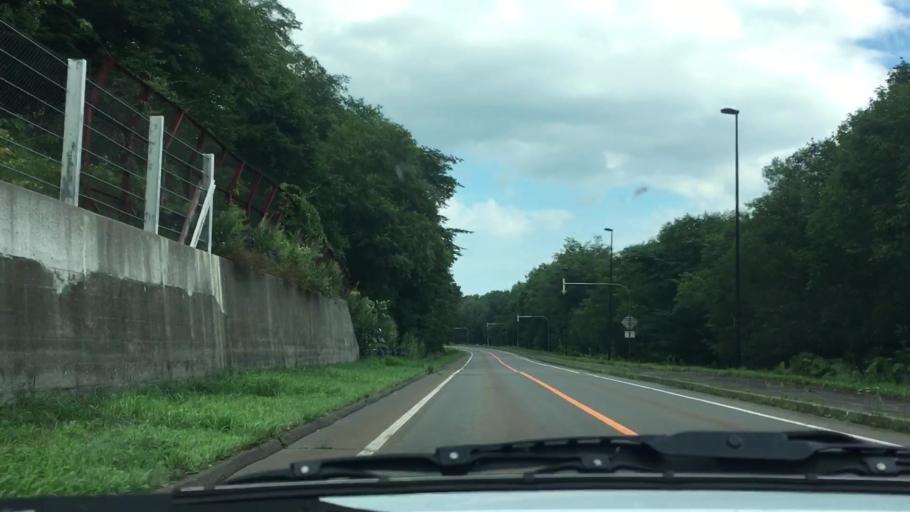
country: JP
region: Hokkaido
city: Otofuke
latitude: 43.3529
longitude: 143.2630
